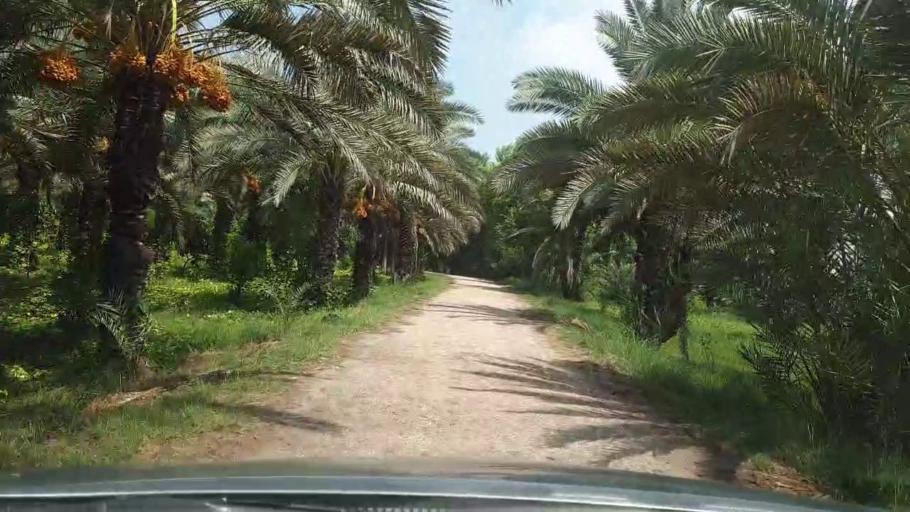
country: PK
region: Sindh
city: Pir jo Goth
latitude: 27.6155
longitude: 68.6664
